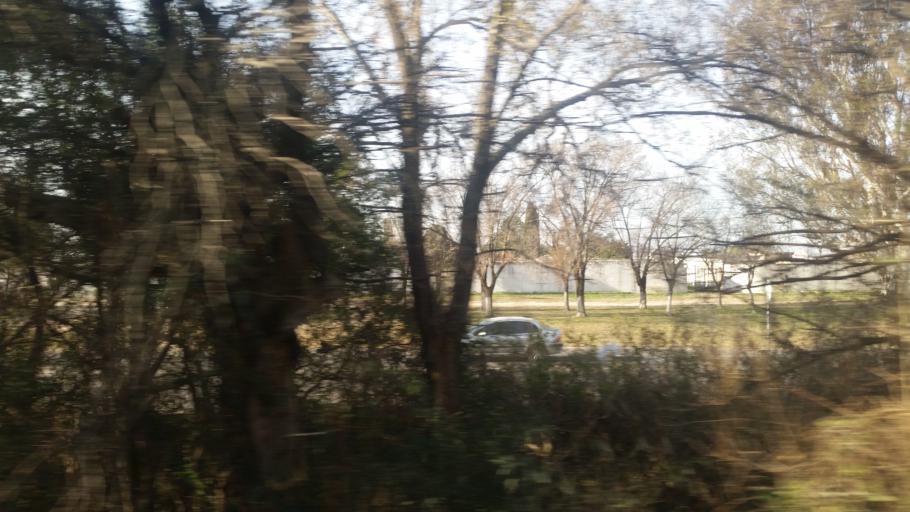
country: AR
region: Cordoba
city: Toledo
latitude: -31.5732
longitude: -63.9920
